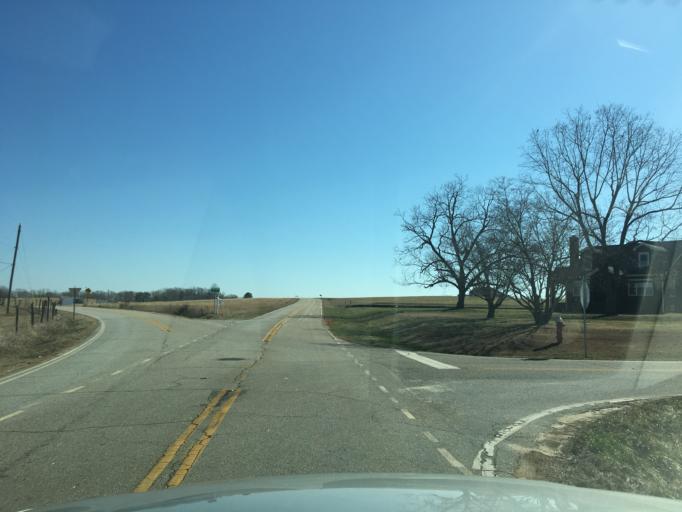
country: US
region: South Carolina
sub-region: Pickens County
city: Liberty
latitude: 34.8194
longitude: -82.7780
